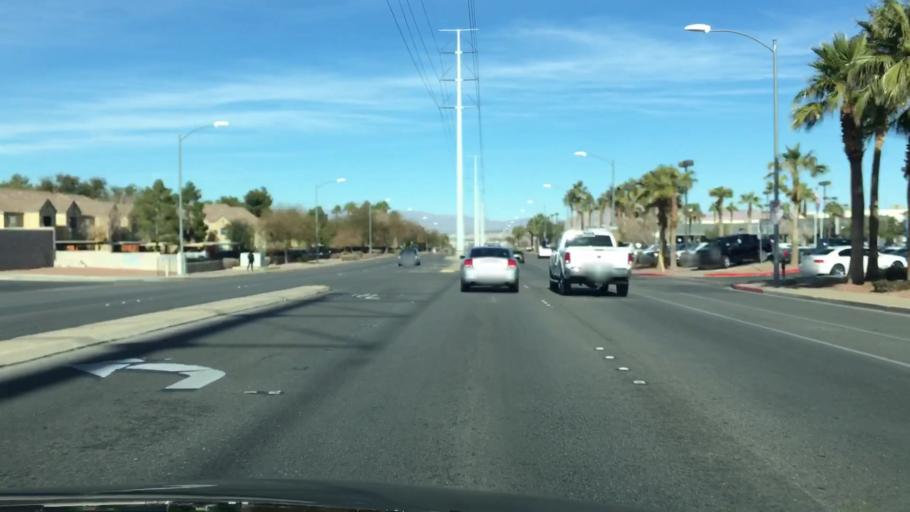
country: US
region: Nevada
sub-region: Clark County
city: Henderson
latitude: 36.0485
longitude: -115.0290
